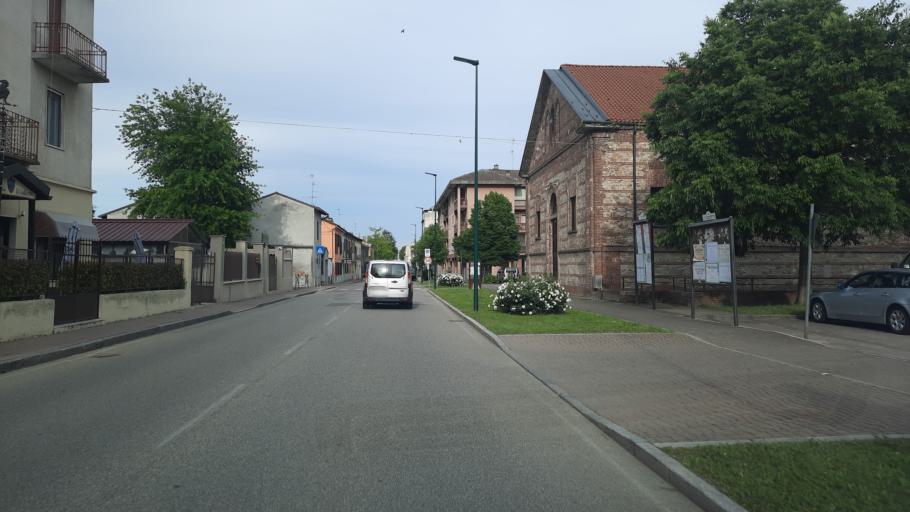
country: IT
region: Piedmont
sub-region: Provincia di Alessandria
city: Casale Monferrato
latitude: 45.1359
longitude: 8.4388
